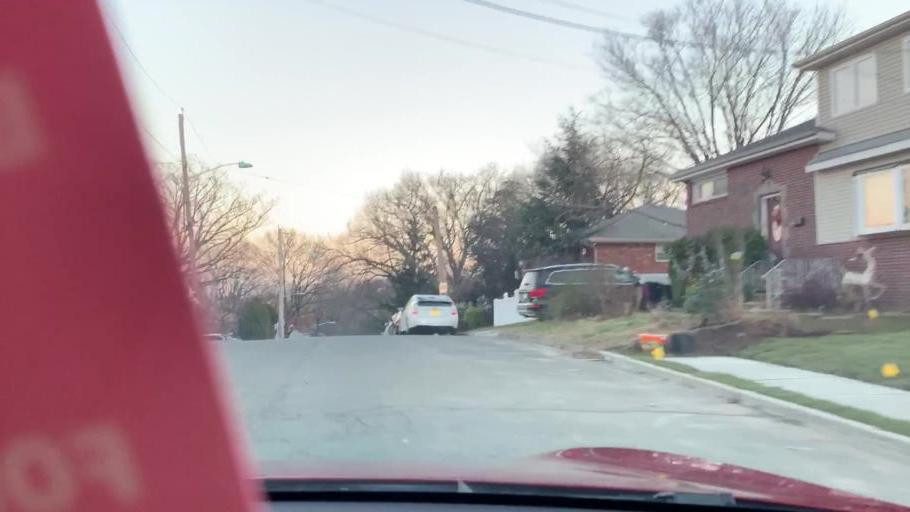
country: US
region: New Jersey
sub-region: Bergen County
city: Palisades Park
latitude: 40.8388
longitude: -73.9879
